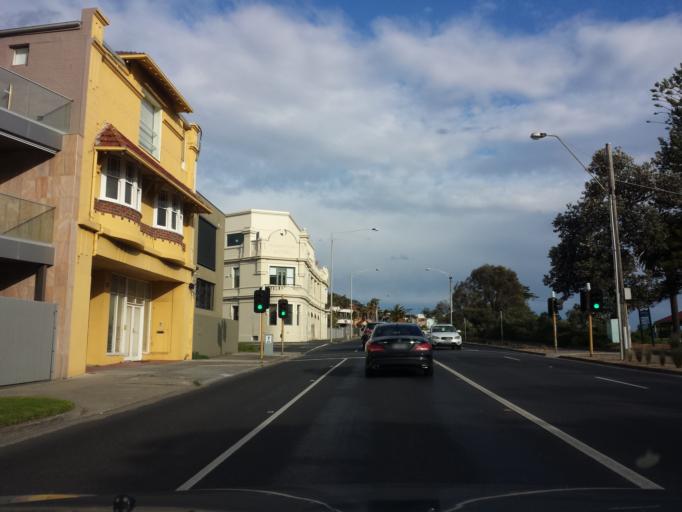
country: AU
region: Victoria
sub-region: Bayside
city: Hampton
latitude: -37.9387
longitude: 144.9991
